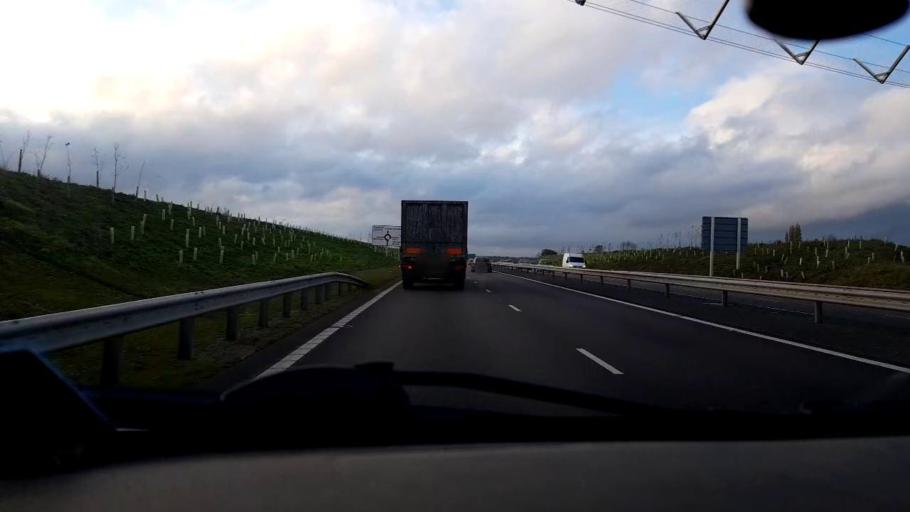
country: GB
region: England
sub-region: Norfolk
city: Horsford
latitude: 52.6844
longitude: 1.2472
